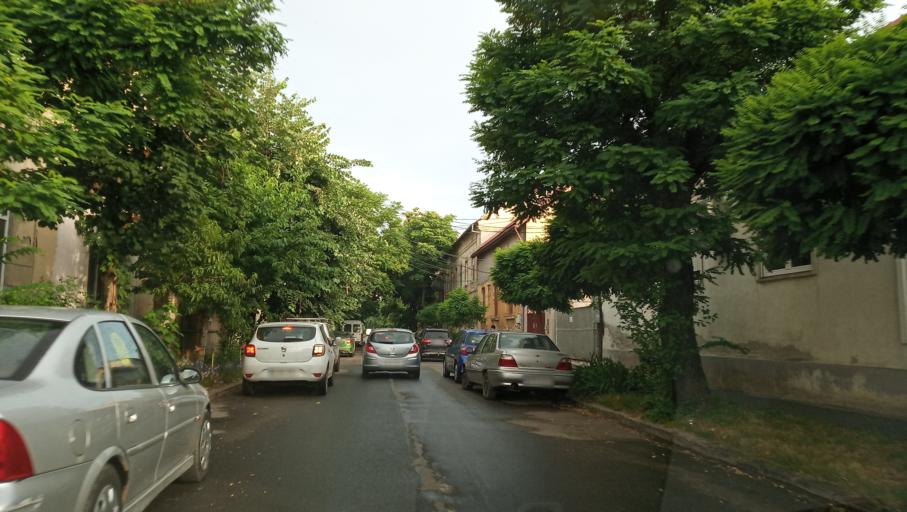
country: RO
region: Timis
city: Timisoara
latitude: 45.7393
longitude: 21.2284
